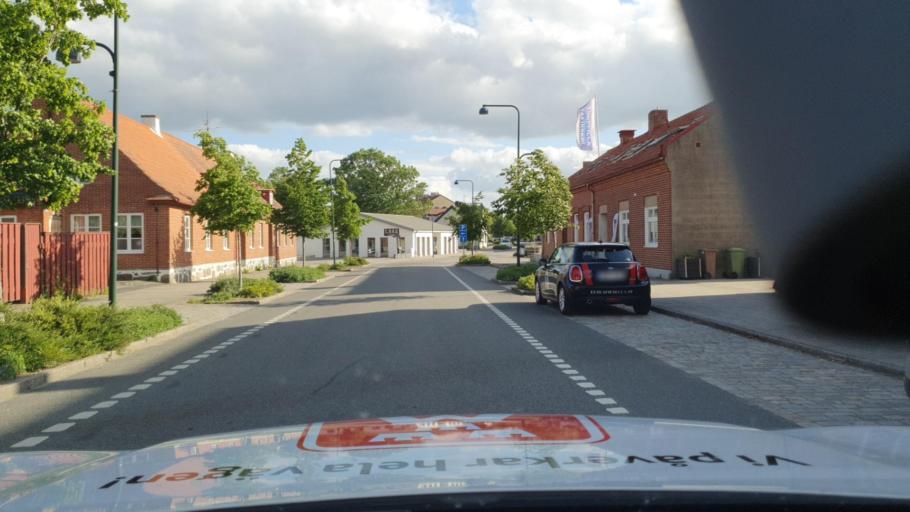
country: SE
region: Skane
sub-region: Tomelilla Kommun
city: Tomelilla
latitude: 55.5469
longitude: 13.9523
